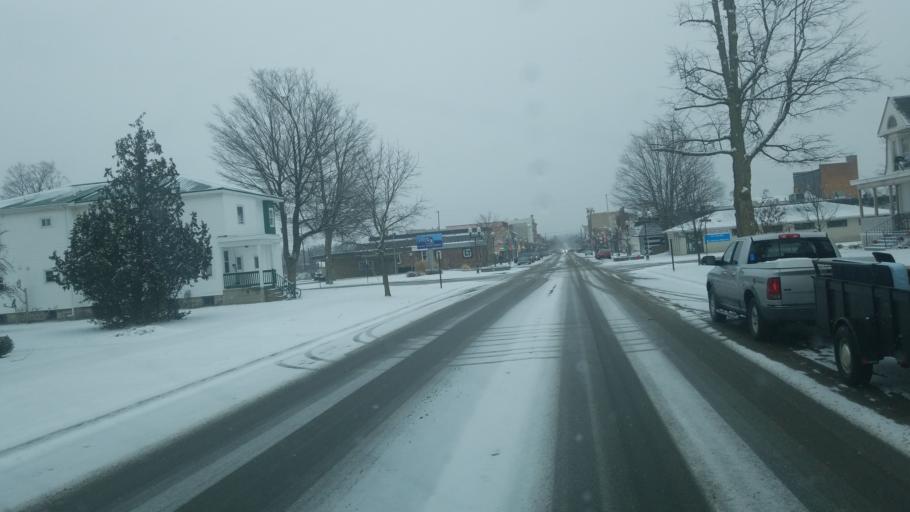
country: US
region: Michigan
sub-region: Mecosta County
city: Big Rapids
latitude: 43.6951
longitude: -85.4819
